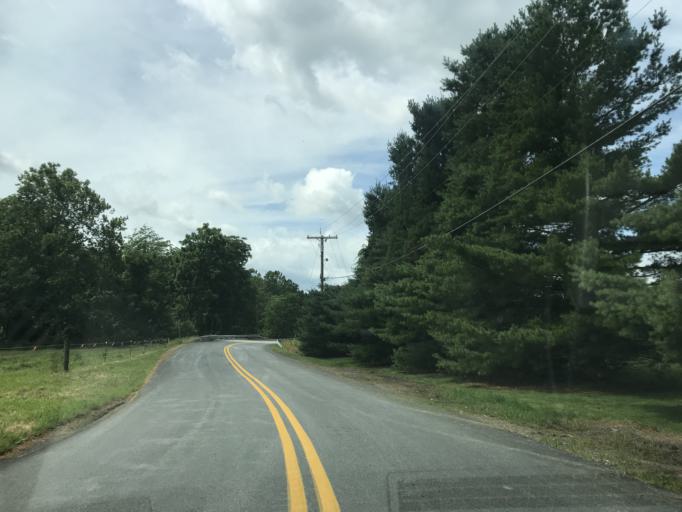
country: US
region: Maryland
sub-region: Carroll County
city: Hampstead
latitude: 39.6167
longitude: -76.7922
